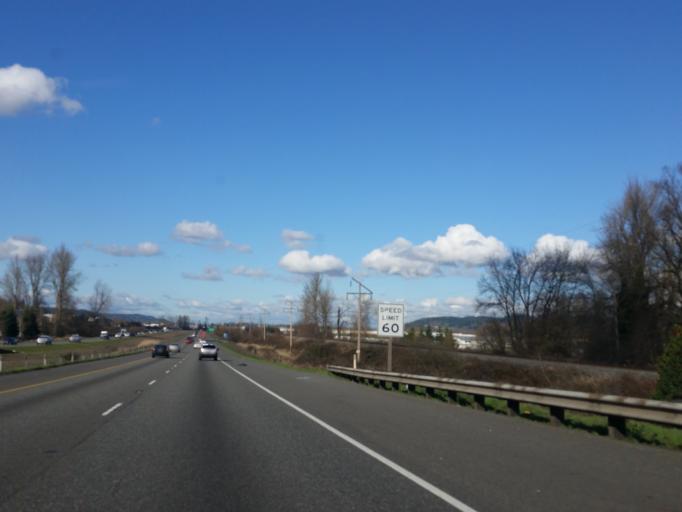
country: US
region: Washington
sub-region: Pierce County
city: Sumner
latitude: 47.2100
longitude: -122.2467
